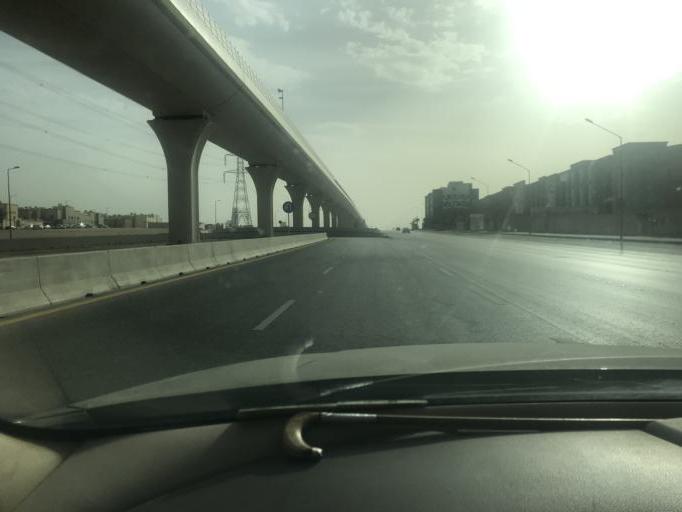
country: SA
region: Ar Riyad
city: Riyadh
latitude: 24.7988
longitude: 46.6896
